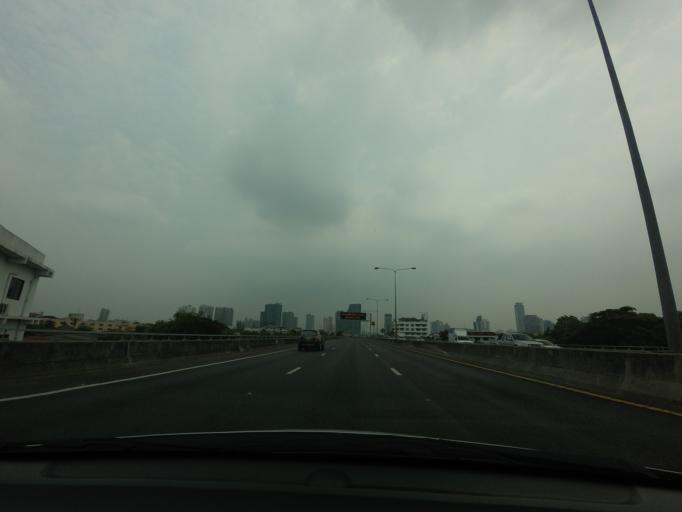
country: TH
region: Bangkok
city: Phra Khanong
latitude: 13.7216
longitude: 100.6042
